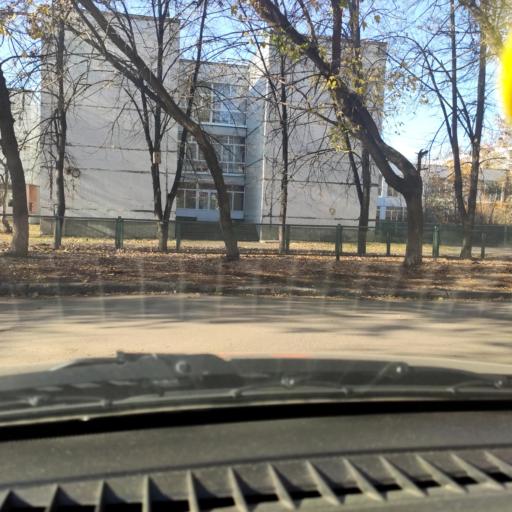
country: RU
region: Samara
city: Tol'yatti
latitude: 53.5352
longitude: 49.2939
